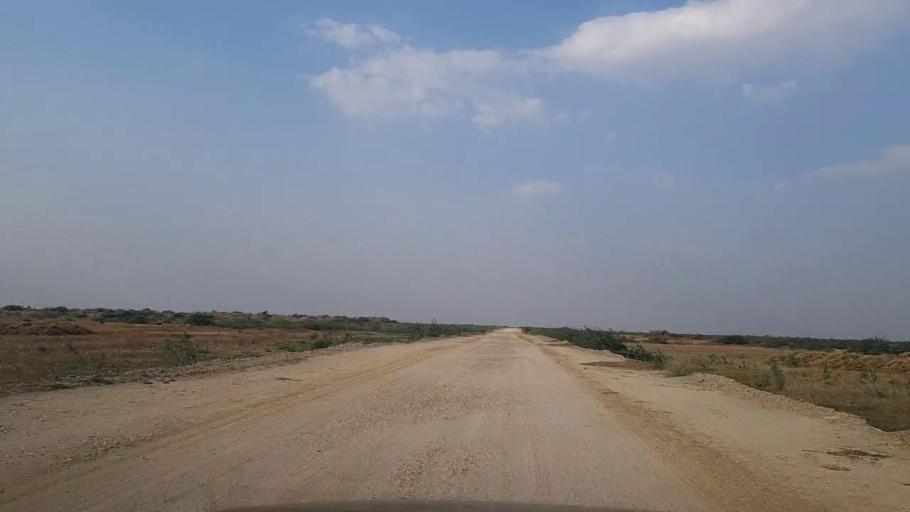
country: PK
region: Sindh
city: Gharo
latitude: 24.8300
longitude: 67.7452
